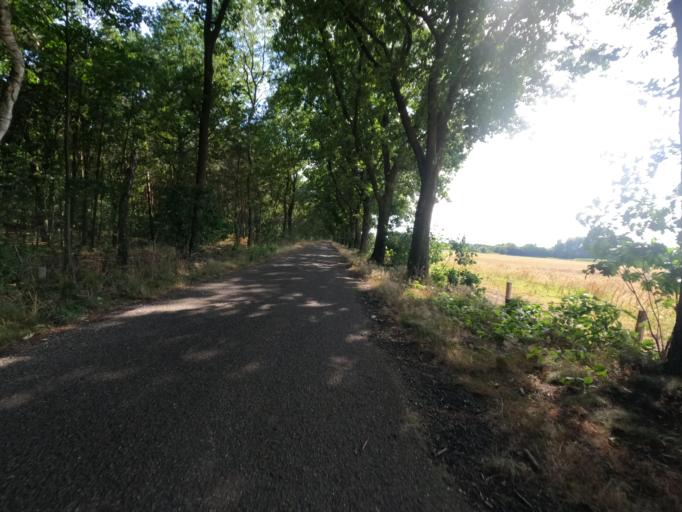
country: NL
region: Limburg
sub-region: Gemeente Beesel
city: Offenbeek
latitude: 51.2643
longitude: 6.1096
